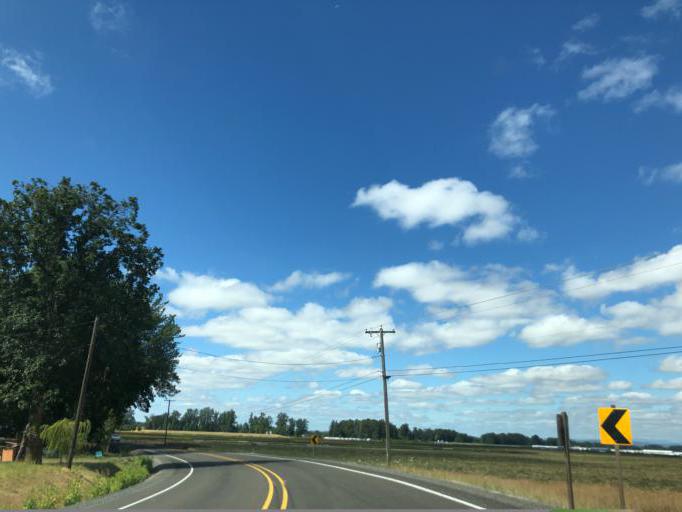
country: US
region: Oregon
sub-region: Marion County
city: Silverton
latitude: 45.0426
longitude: -122.7511
